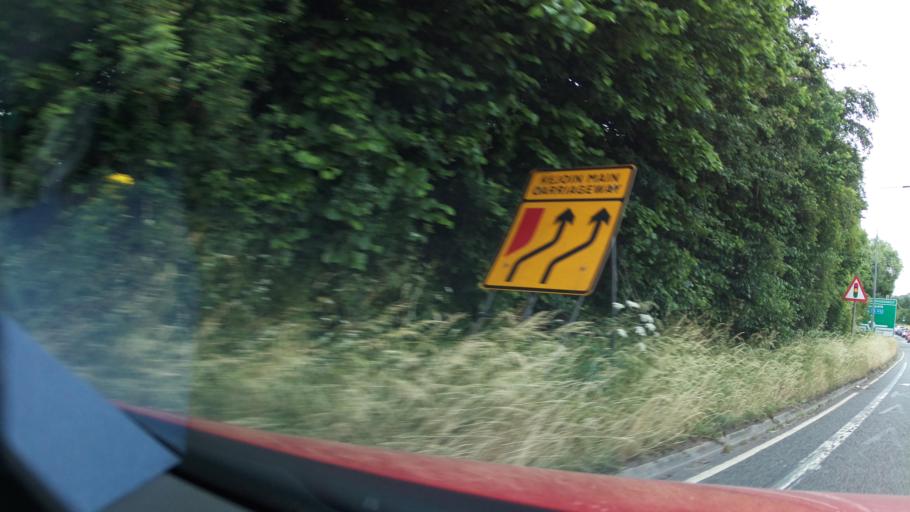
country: GB
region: England
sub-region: South Gloucestershire
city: Kingswood
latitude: 51.4579
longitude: -2.4821
